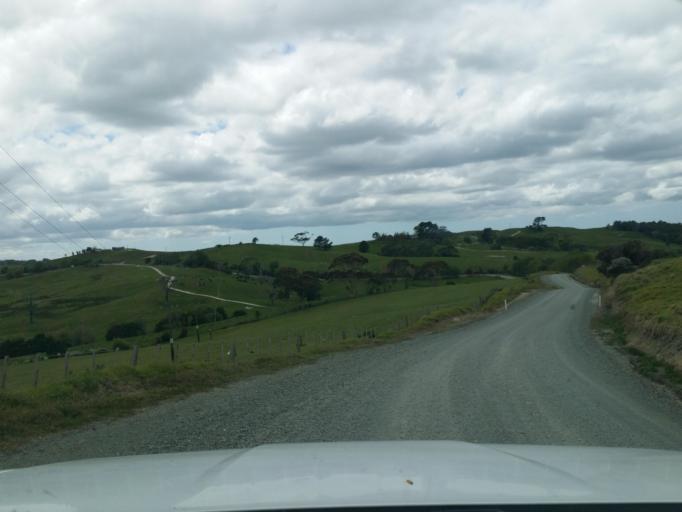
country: NZ
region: Auckland
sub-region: Auckland
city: Wellsford
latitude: -36.2768
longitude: 174.3663
